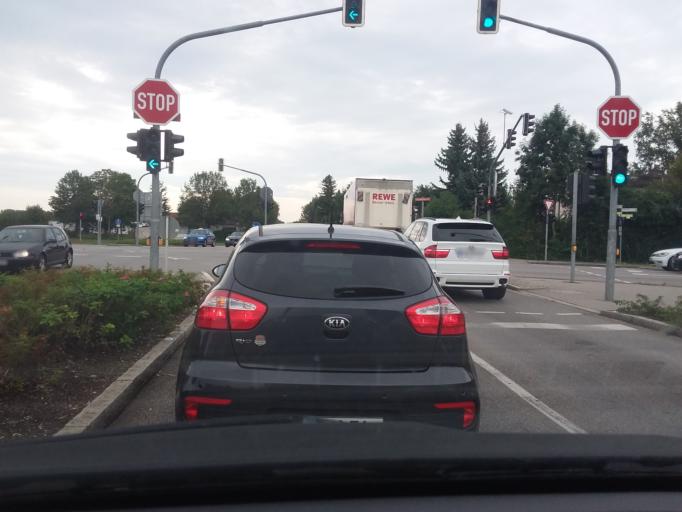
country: DE
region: Bavaria
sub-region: Upper Bavaria
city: Hebertshausen
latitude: 48.2563
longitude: 11.4704
